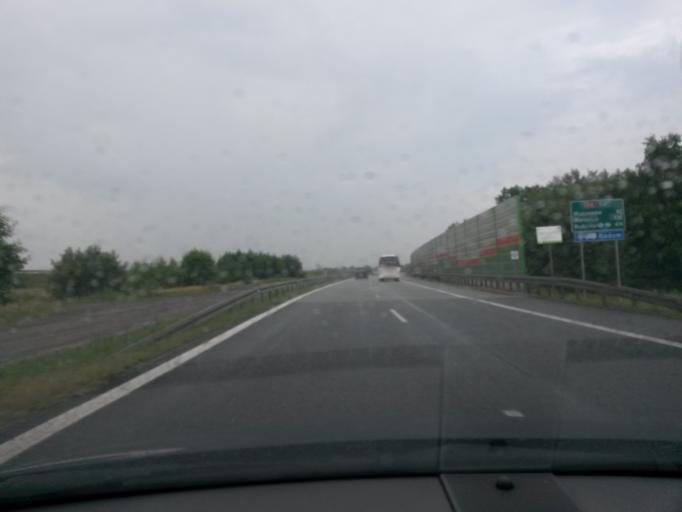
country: PL
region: Lodz Voivodeship
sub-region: Piotrkow Trybunalski
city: Piotrkow Trybunalski
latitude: 51.4359
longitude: 19.6441
